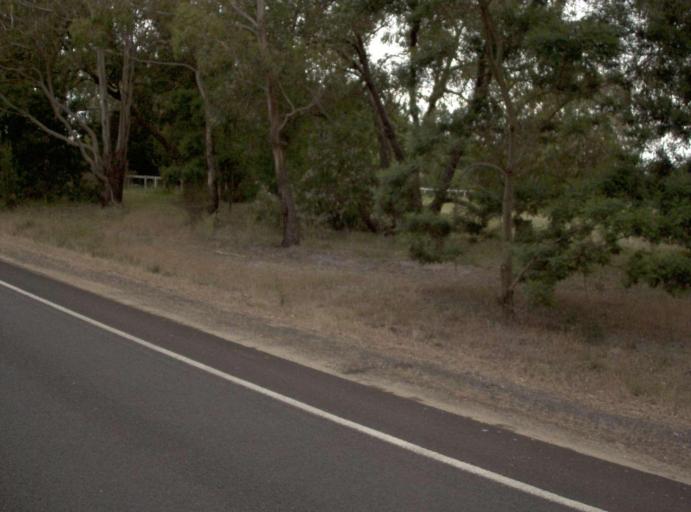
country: AU
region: Victoria
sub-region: Wellington
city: Sale
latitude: -38.4926
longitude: 146.9070
